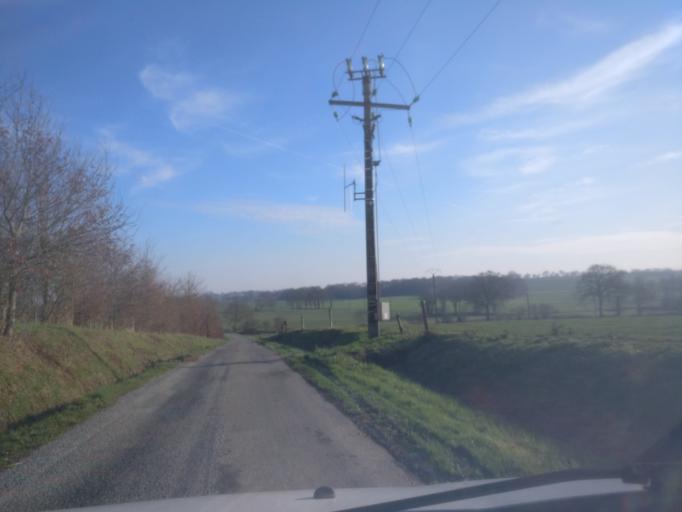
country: FR
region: Brittany
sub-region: Departement d'Ille-et-Vilaine
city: Livre-sur-Changeon
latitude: 48.2199
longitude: -1.3230
